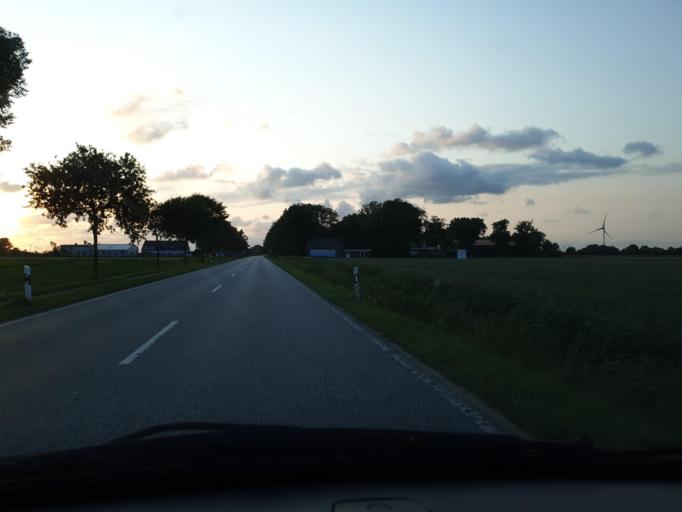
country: DE
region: Schleswig-Holstein
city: Schmedeswurth
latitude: 53.9237
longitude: 9.0433
